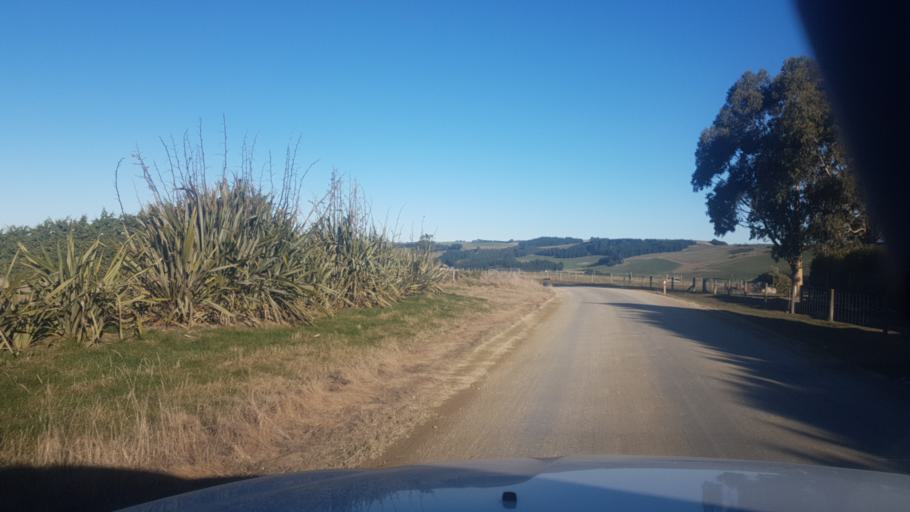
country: NZ
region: Canterbury
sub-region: Timaru District
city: Pleasant Point
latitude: -44.3611
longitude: 171.0696
